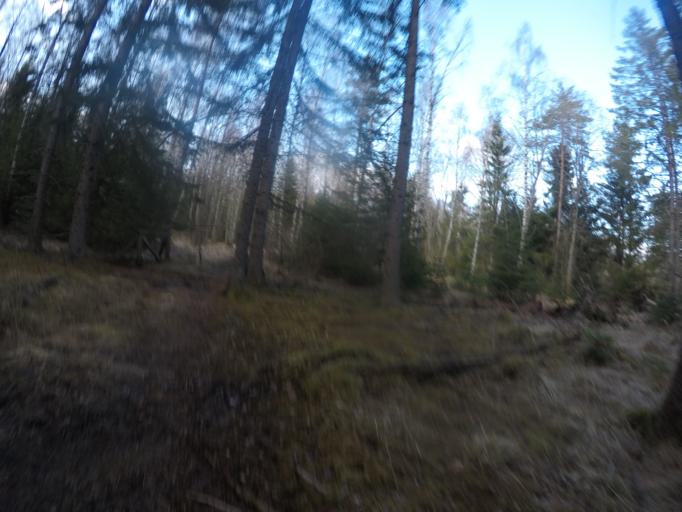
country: SE
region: Soedermanland
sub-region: Eskilstuna Kommun
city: Hallbybrunn
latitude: 59.3906
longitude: 16.4023
